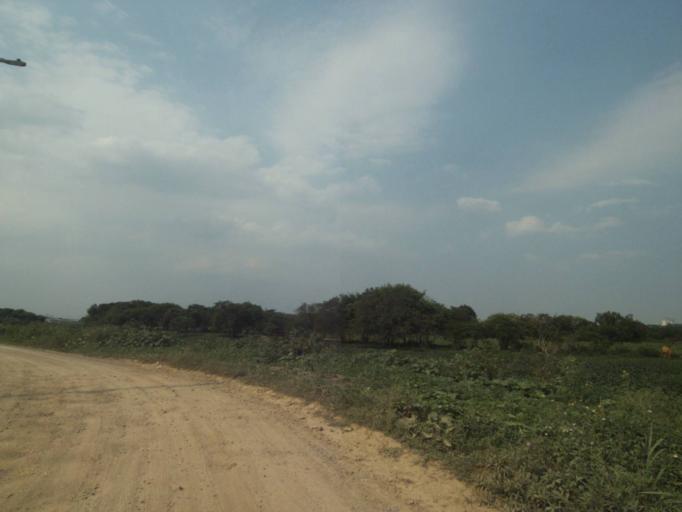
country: BR
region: Parana
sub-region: Sao Jose Dos Pinhais
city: Sao Jose dos Pinhais
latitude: -25.5413
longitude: -49.2323
